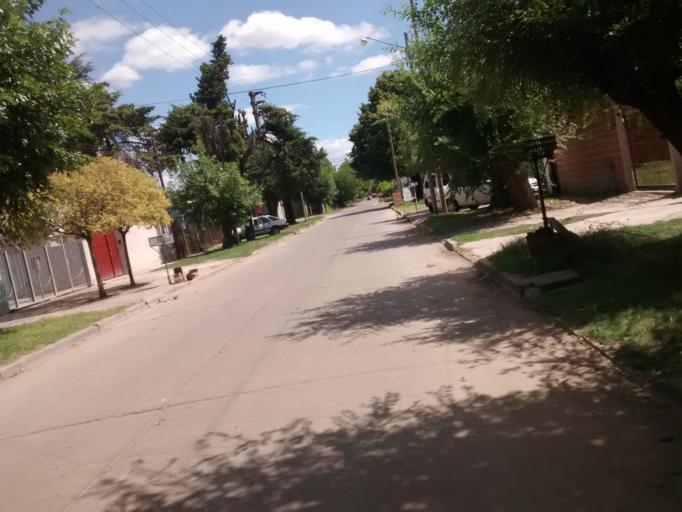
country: AR
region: Buenos Aires
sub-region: Partido de La Plata
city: La Plata
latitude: -34.9252
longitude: -58.0042
